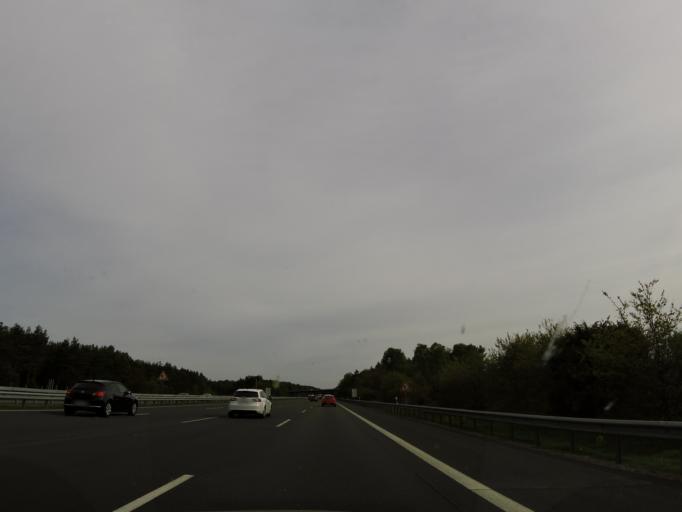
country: DE
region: Lower Saxony
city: Hademstorf
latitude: 52.7816
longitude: 9.6704
